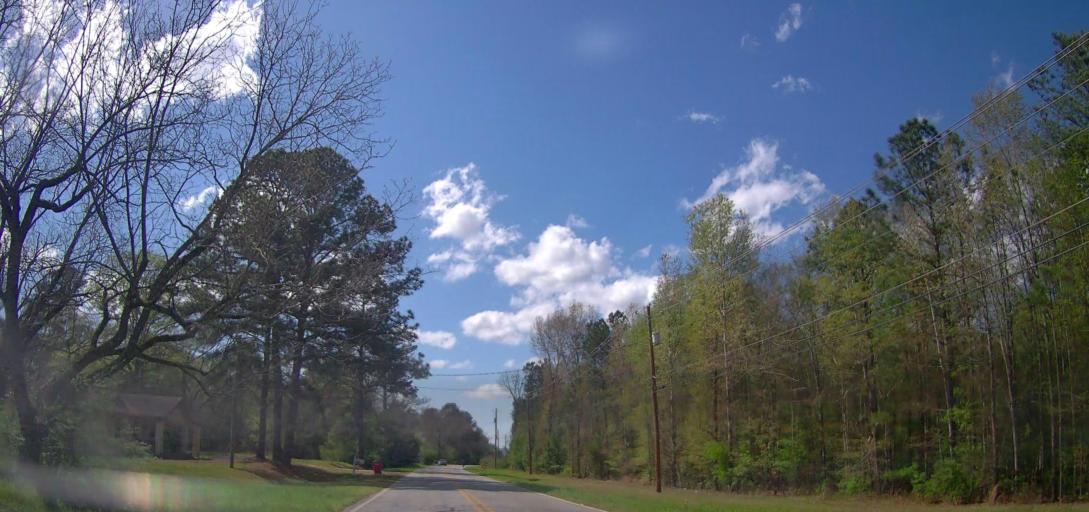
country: US
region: Georgia
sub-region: Bibb County
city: Macon
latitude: 32.8344
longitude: -83.5648
